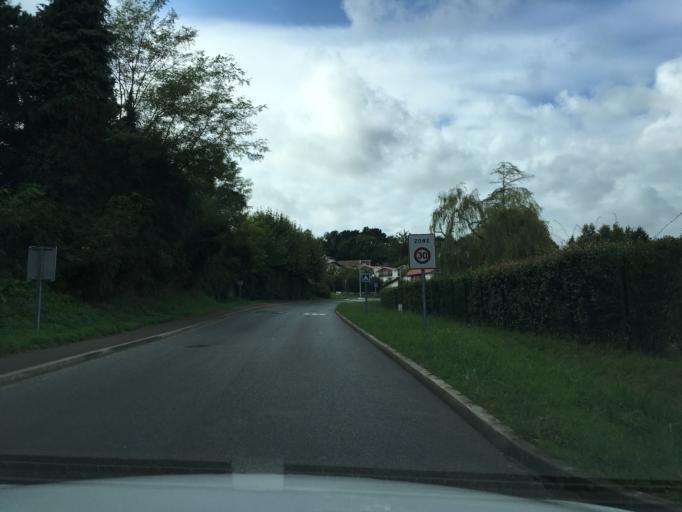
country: FR
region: Aquitaine
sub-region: Departement des Pyrenees-Atlantiques
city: Bassussarry
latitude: 43.4543
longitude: -1.4964
